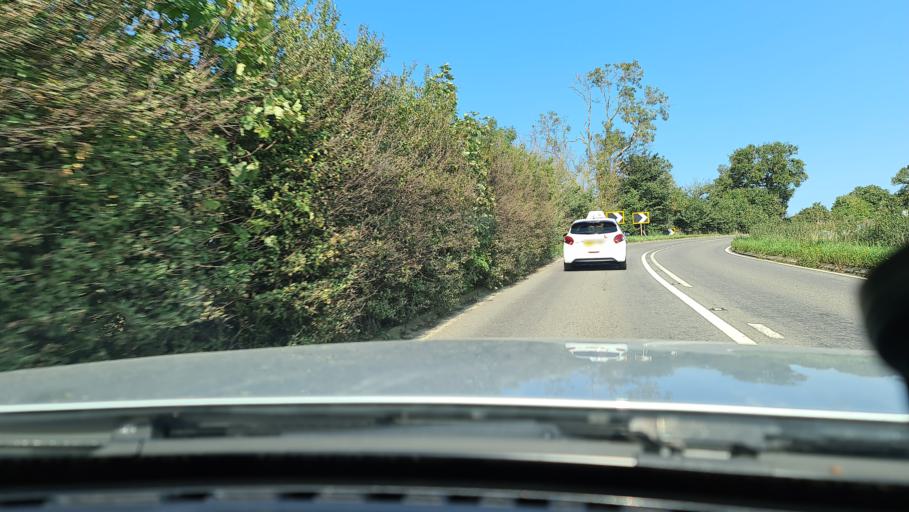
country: GB
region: England
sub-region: Northamptonshire
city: Daventry
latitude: 52.2843
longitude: -1.1695
